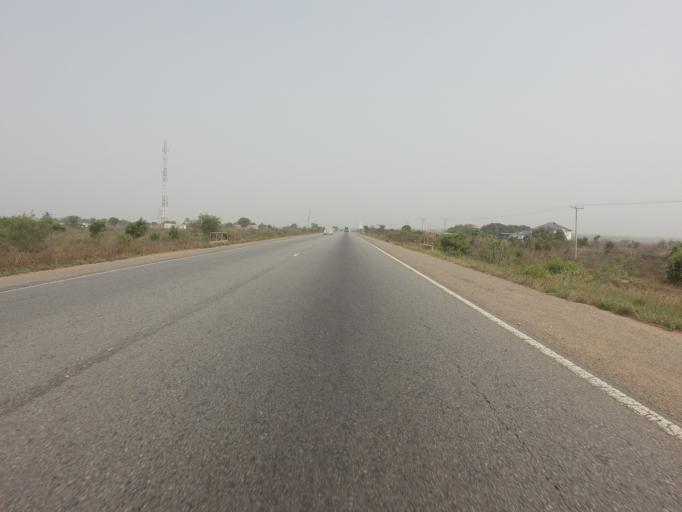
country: GH
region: Greater Accra
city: Tema
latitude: 5.8668
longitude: 0.2962
